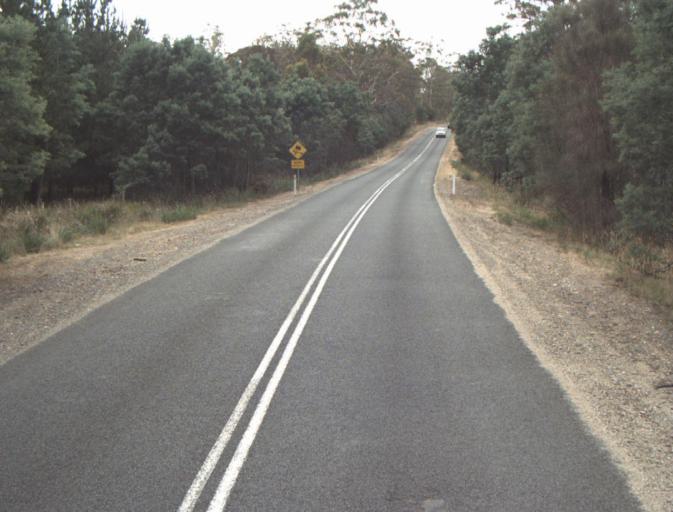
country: AU
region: Tasmania
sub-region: Northern Midlands
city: Evandale
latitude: -41.5082
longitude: 147.3516
